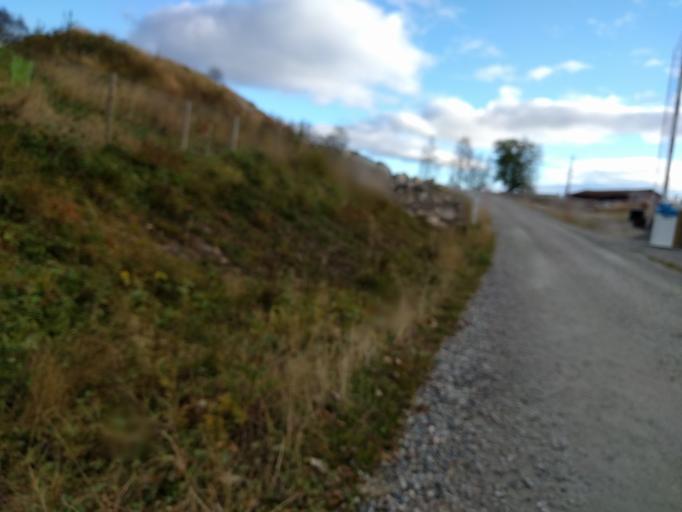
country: NO
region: Aust-Agder
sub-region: Evje og Hornnes
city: Evje
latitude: 58.6517
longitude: 7.9497
